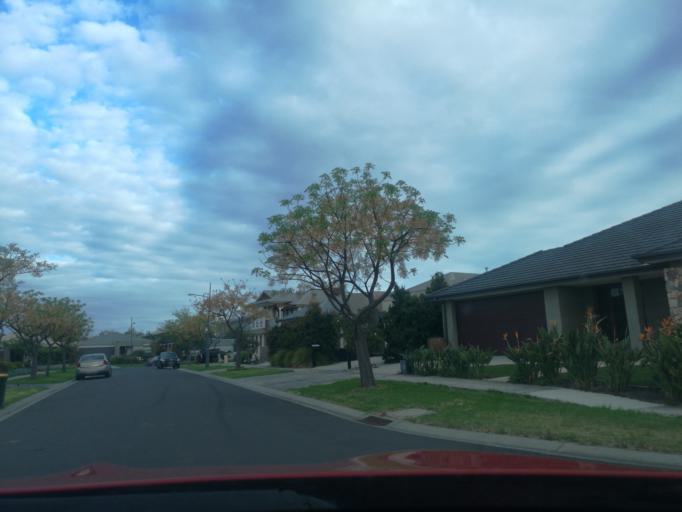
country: AU
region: Victoria
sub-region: Wyndham
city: Point Cook
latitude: -37.9125
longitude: 144.7761
